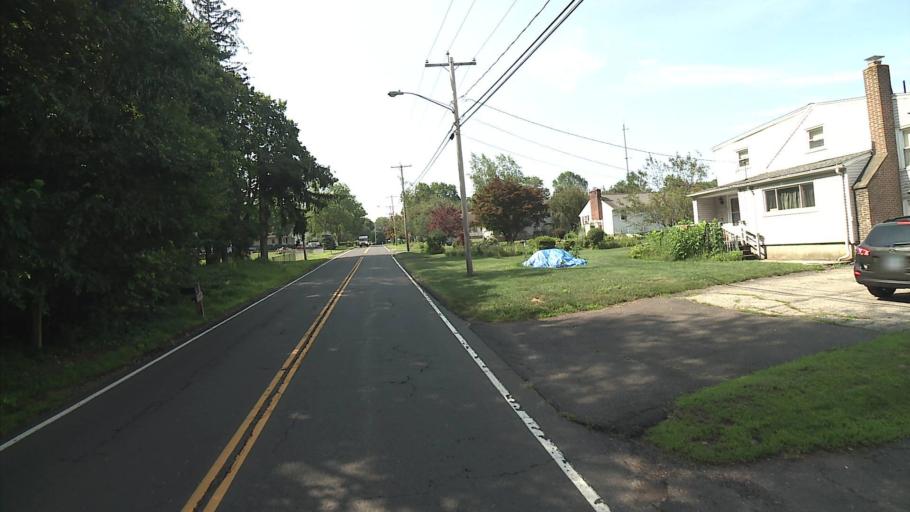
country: US
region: Connecticut
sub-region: New Haven County
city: Wolcott
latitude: 41.5659
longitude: -72.9475
